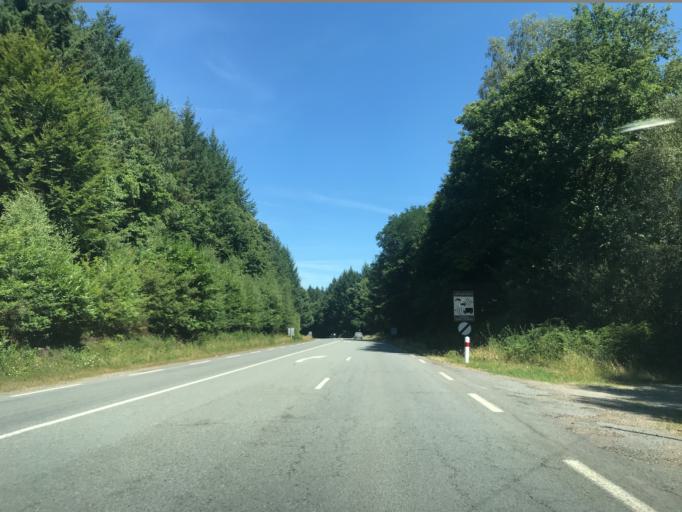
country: FR
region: Limousin
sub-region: Departement de la Correze
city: Egletons
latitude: 45.3632
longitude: 1.9901
